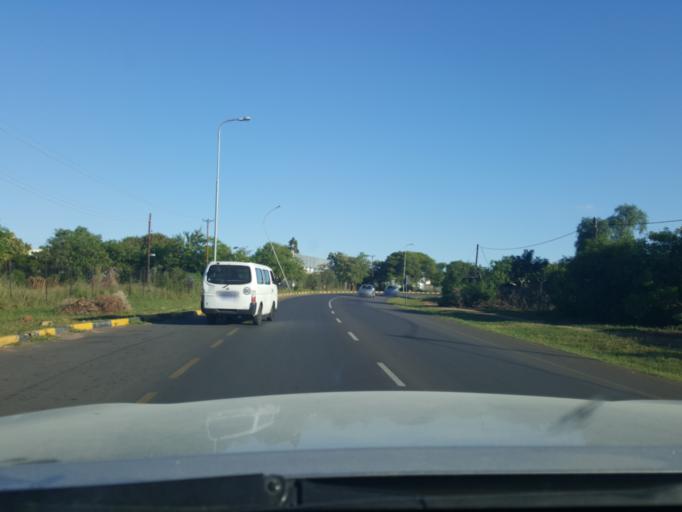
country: BW
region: South East
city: Gaborone
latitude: -24.6397
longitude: 25.9396
